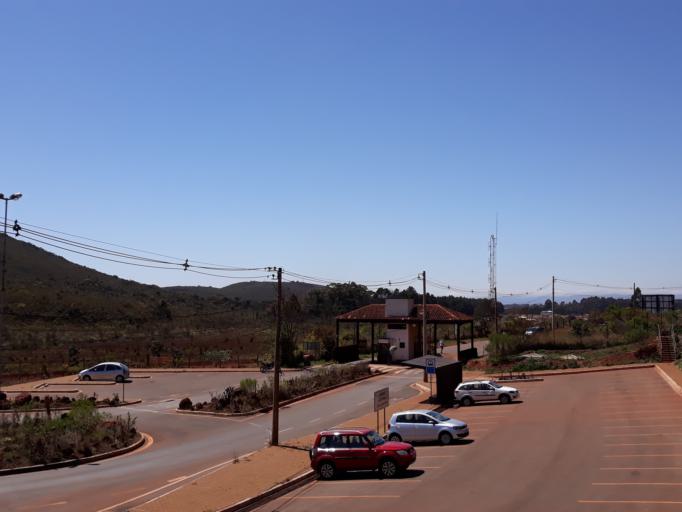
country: BR
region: Minas Gerais
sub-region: Ibirite
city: Ibirite
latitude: -20.0522
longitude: -44.0008
